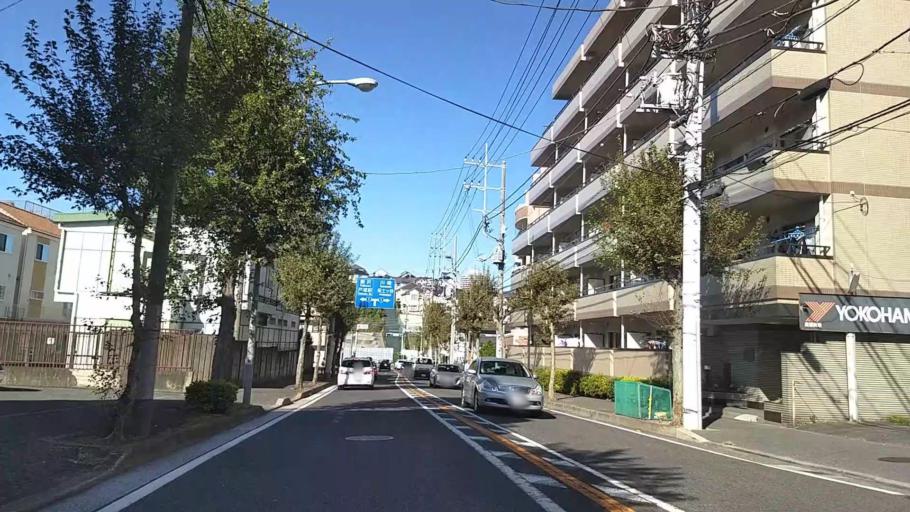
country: JP
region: Kanagawa
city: Yokohama
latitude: 35.4251
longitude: 139.5703
